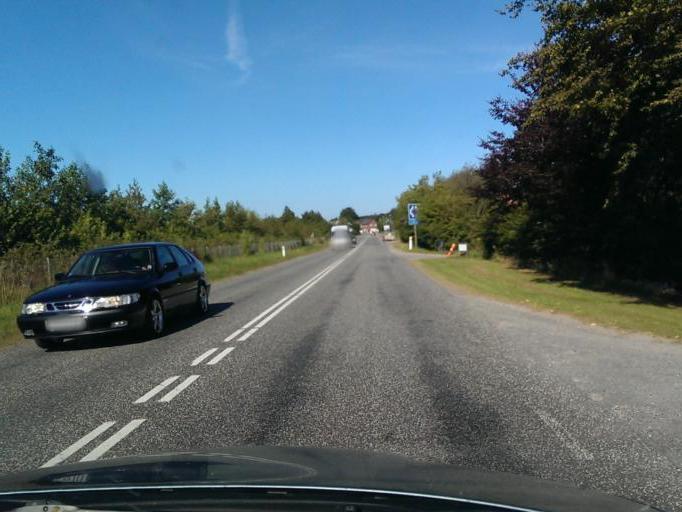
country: DK
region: Central Jutland
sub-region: Odder Kommune
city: Odder
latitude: 55.9235
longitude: 10.1477
